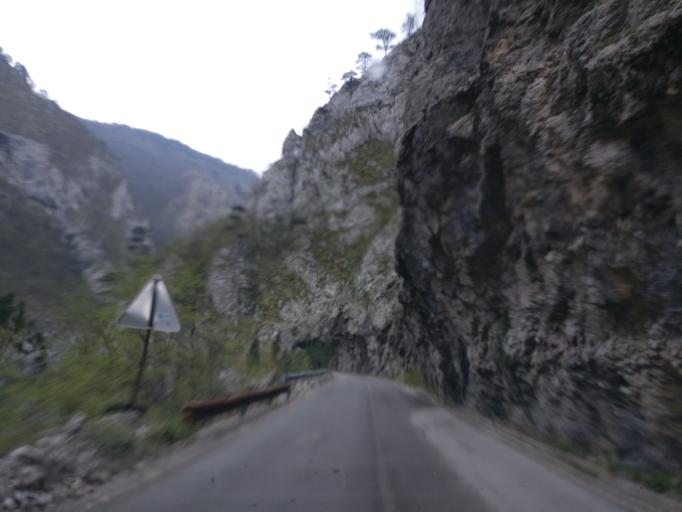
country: ME
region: Opstina Pluzine
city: Pluzine
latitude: 43.2830
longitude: 18.8492
